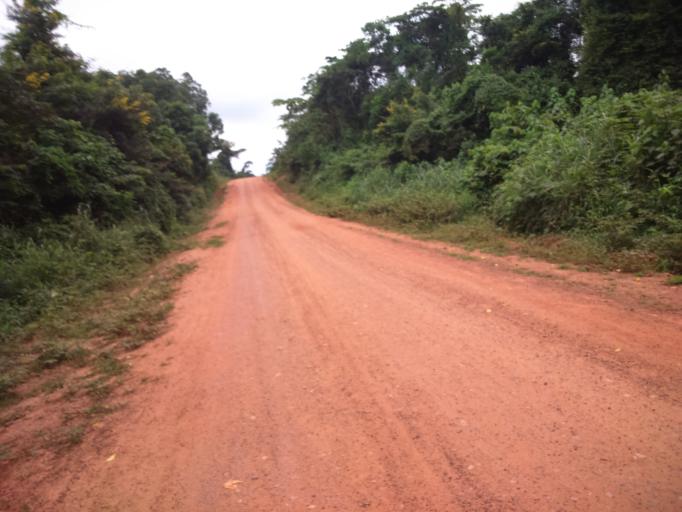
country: CI
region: Lagunes
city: Agou
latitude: 6.0812
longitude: -4.0670
